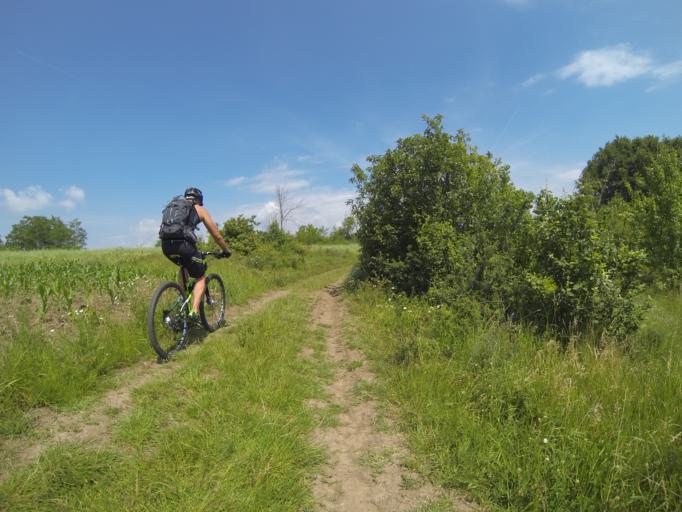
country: RO
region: Gorj
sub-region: Comuna Crusetu
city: Crusetu
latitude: 44.6180
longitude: 23.6234
